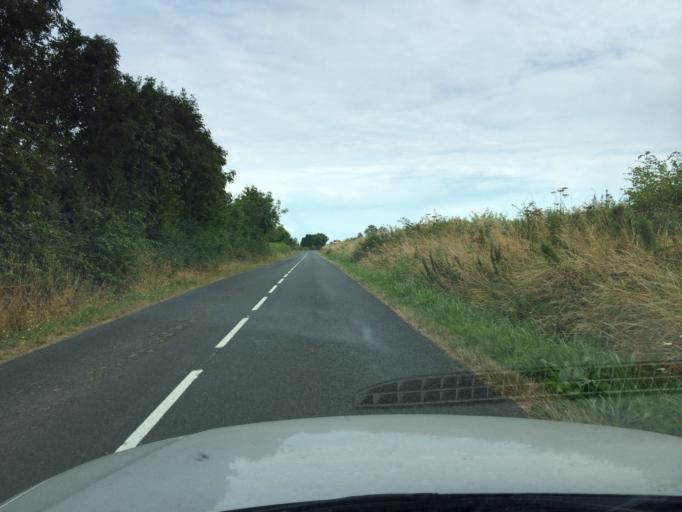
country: FR
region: Lower Normandy
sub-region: Departement de la Manche
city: Sainte-Mere-Eglise
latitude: 49.4337
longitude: -1.2970
